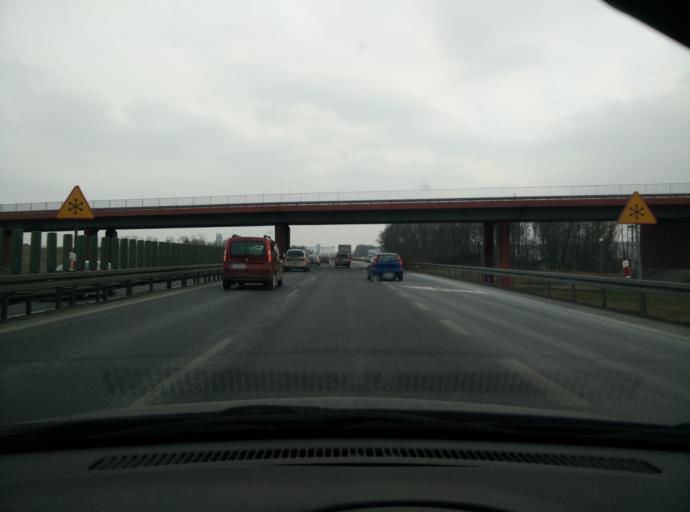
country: PL
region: Greater Poland Voivodeship
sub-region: Powiat poznanski
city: Daszewice
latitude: 52.3236
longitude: 17.0329
